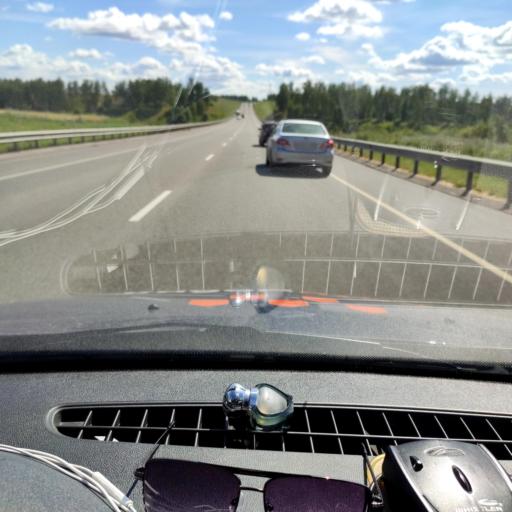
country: RU
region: Lipetsk
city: Borinskoye
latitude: 52.4745
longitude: 39.3922
